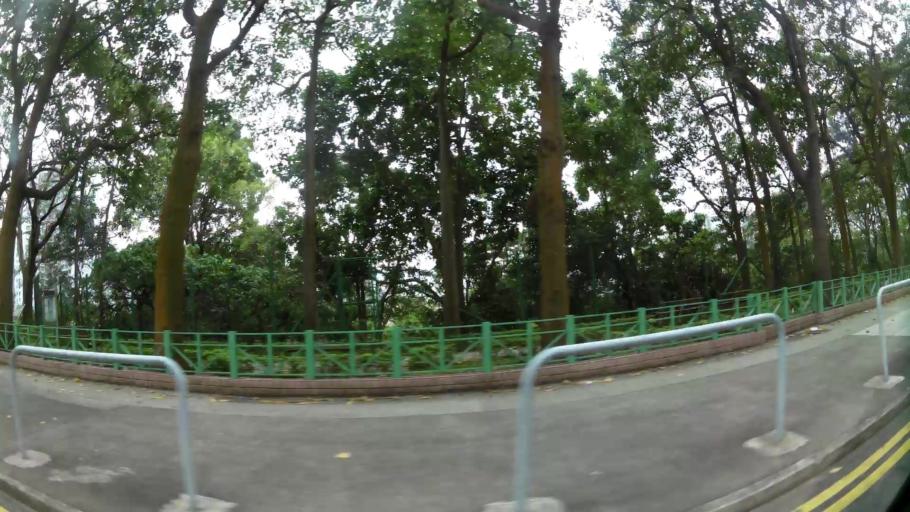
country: HK
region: Wong Tai Sin
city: Wong Tai Sin
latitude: 22.3496
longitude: 114.1956
